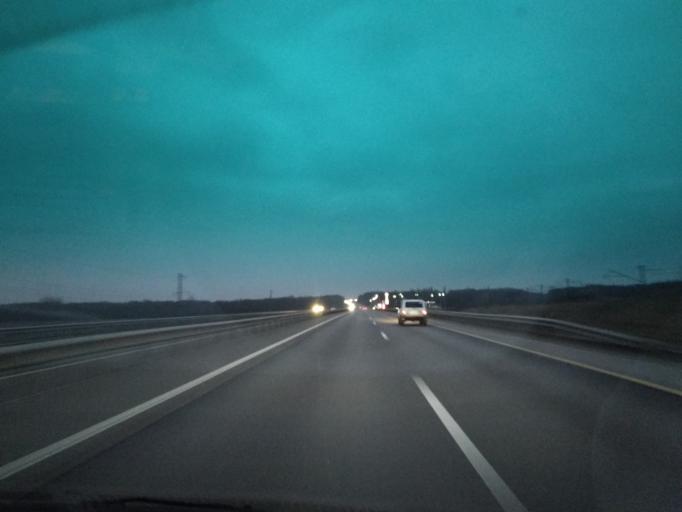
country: RU
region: Krasnodarskiy
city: Saratovskaya
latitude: 44.7966
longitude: 39.2322
